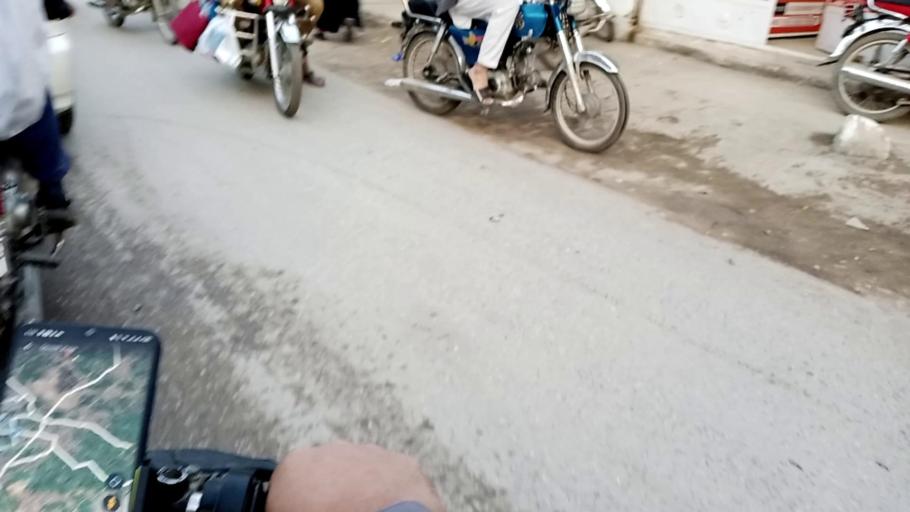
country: PK
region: Khyber Pakhtunkhwa
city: Peshawar
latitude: 34.0237
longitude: 71.4858
